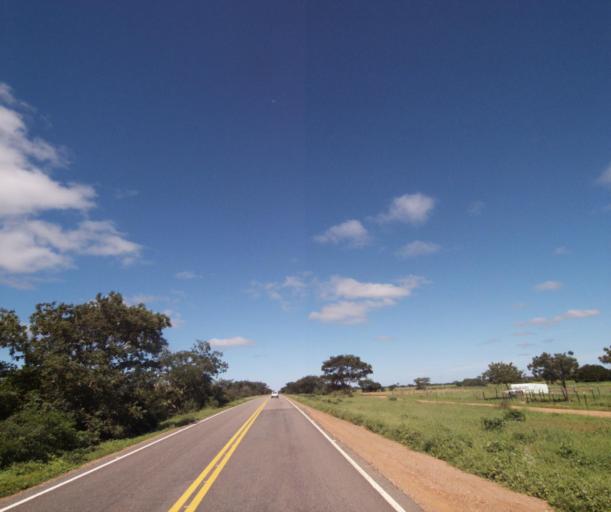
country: BR
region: Bahia
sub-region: Palmas De Monte Alto
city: Palmas de Monte Alto
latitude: -14.2404
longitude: -43.0489
